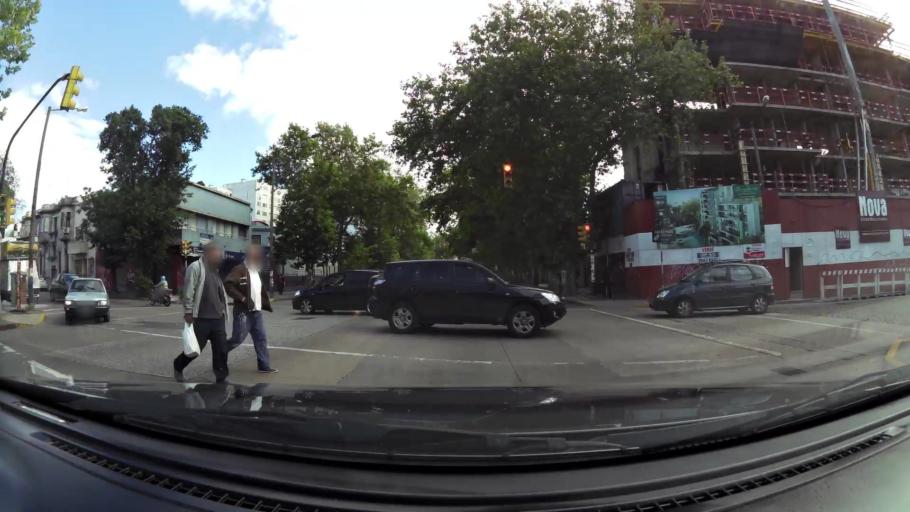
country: UY
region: Montevideo
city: Montevideo
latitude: -34.8852
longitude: -56.1566
